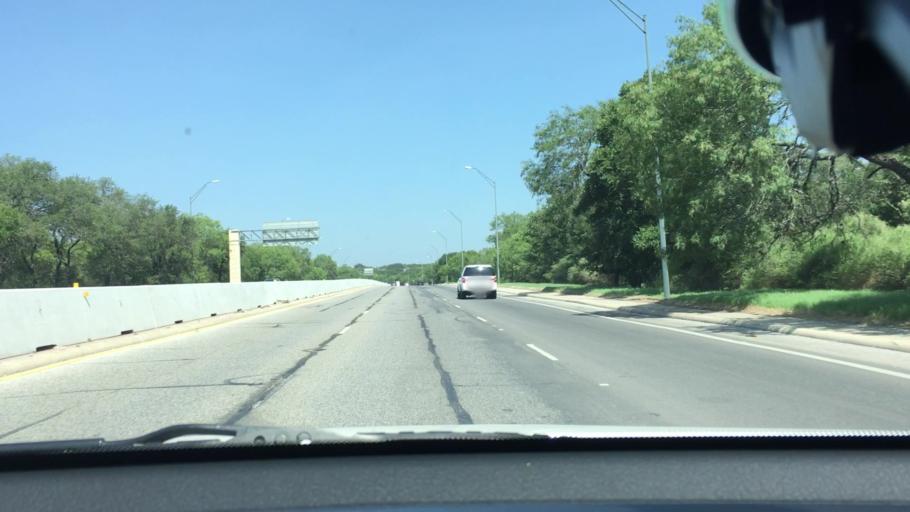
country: US
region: Texas
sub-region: Bexar County
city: Castle Hills
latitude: 29.5587
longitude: -98.5244
